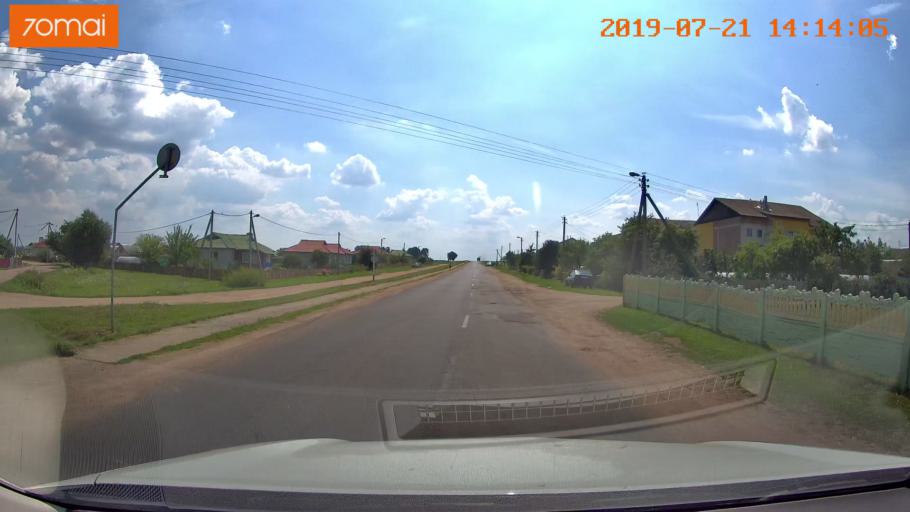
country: BY
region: Grodnenskaya
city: Karelichy
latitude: 53.6503
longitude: 26.1694
